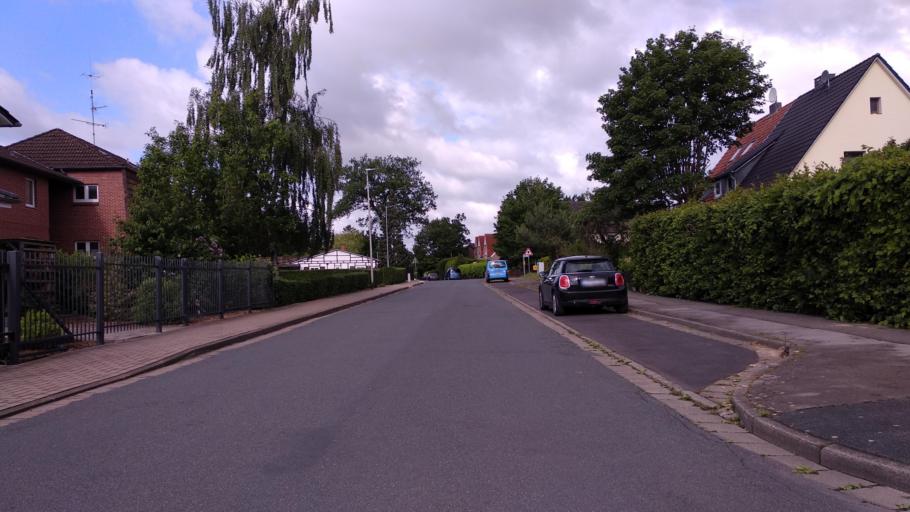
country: DE
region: Lower Saxony
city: Hagenburg
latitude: 52.4596
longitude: 9.3747
